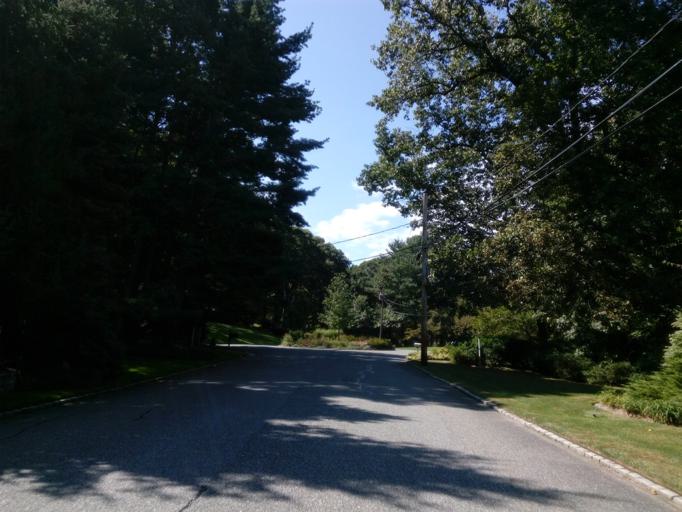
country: US
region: New York
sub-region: Nassau County
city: Oyster Bay Cove
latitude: 40.8579
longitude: -73.4996
